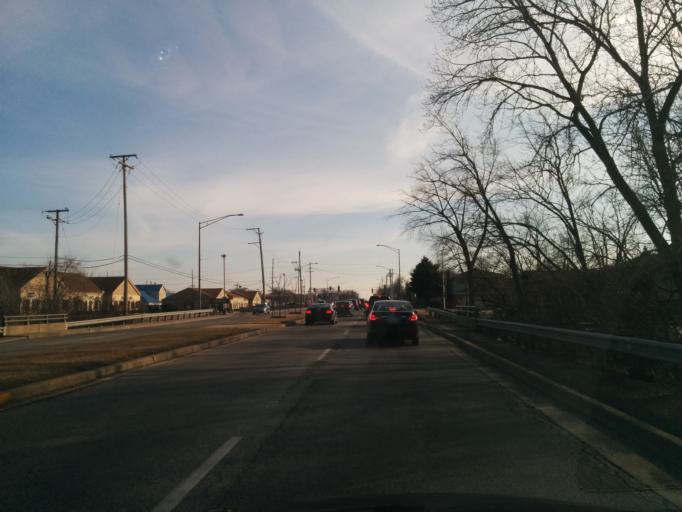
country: US
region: Illinois
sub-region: Cook County
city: Tinley Park
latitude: 41.5825
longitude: -87.7936
